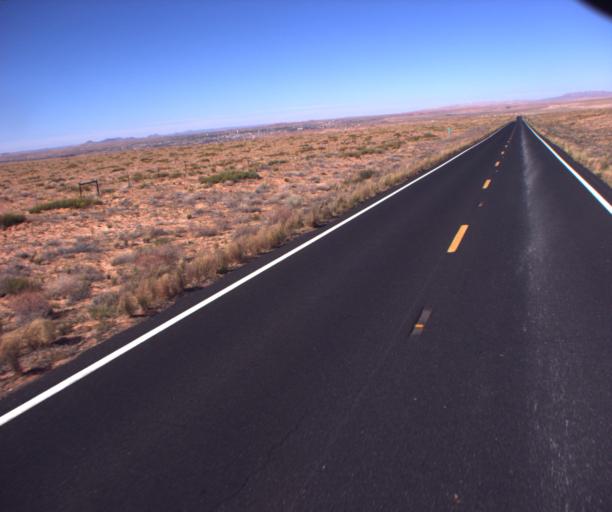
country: US
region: Arizona
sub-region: Coconino County
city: Tuba City
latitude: 36.0662
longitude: -111.1833
